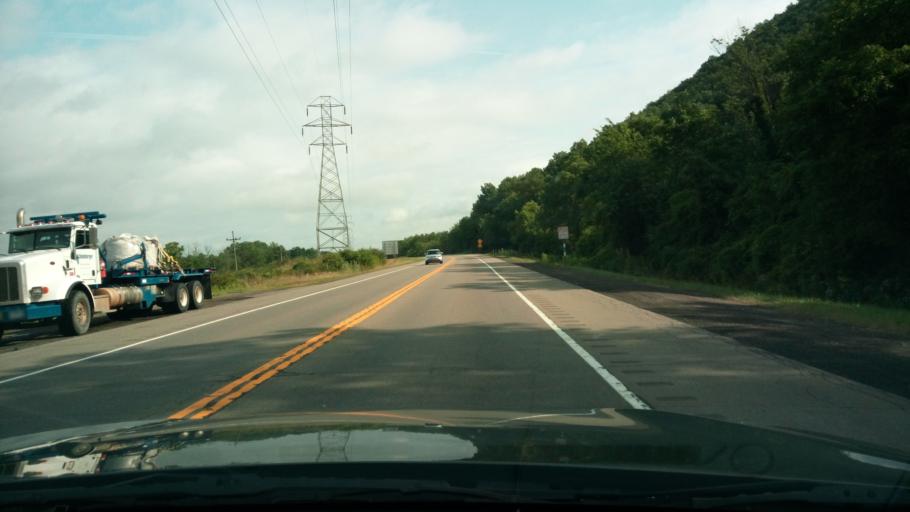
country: US
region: New York
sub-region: Chemung County
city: Horseheads
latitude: 42.1583
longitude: -76.8054
